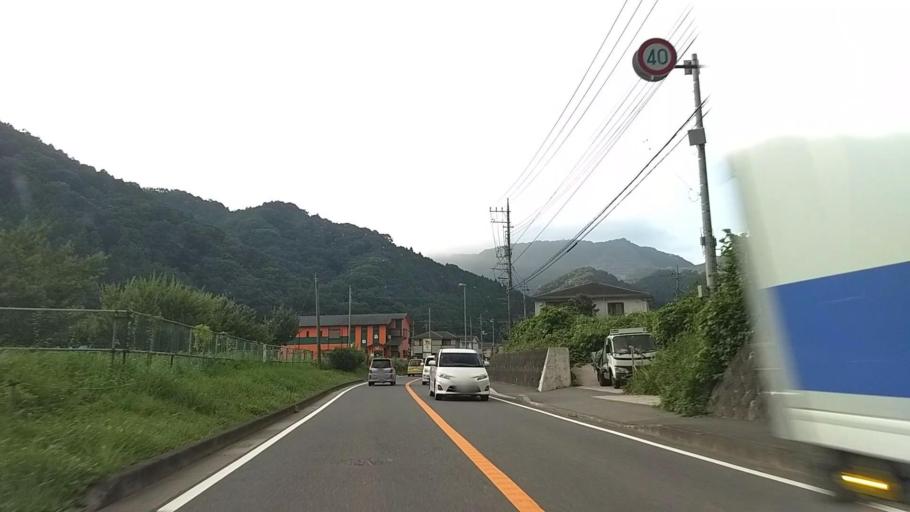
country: JP
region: Kanagawa
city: Atsugi
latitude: 35.4747
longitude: 139.2942
